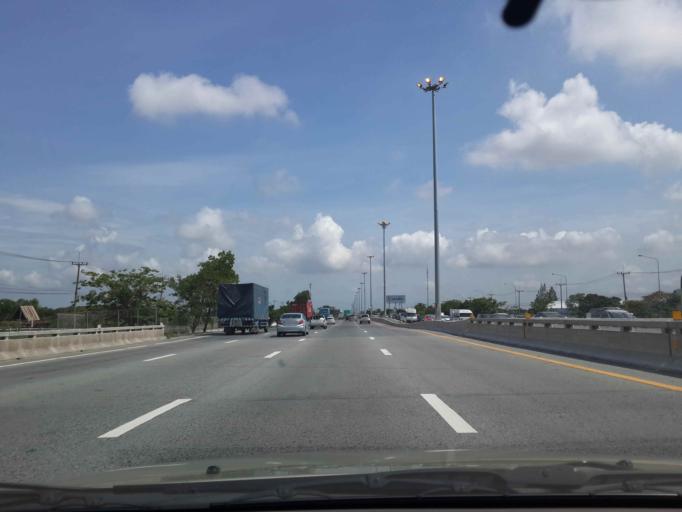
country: TH
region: Chachoengsao
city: Bang Pakong
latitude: 13.5284
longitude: 101.0180
